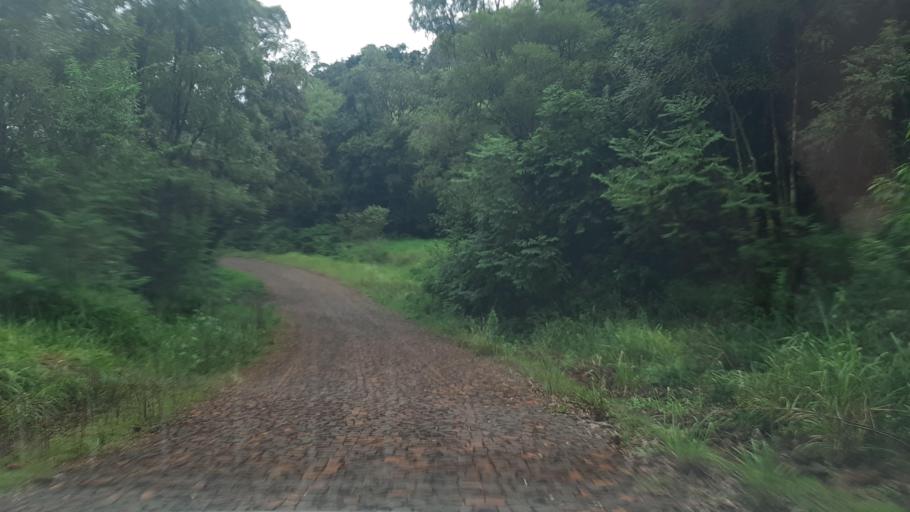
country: BR
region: Parana
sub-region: Ampere
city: Ampere
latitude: -26.0419
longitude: -53.5143
